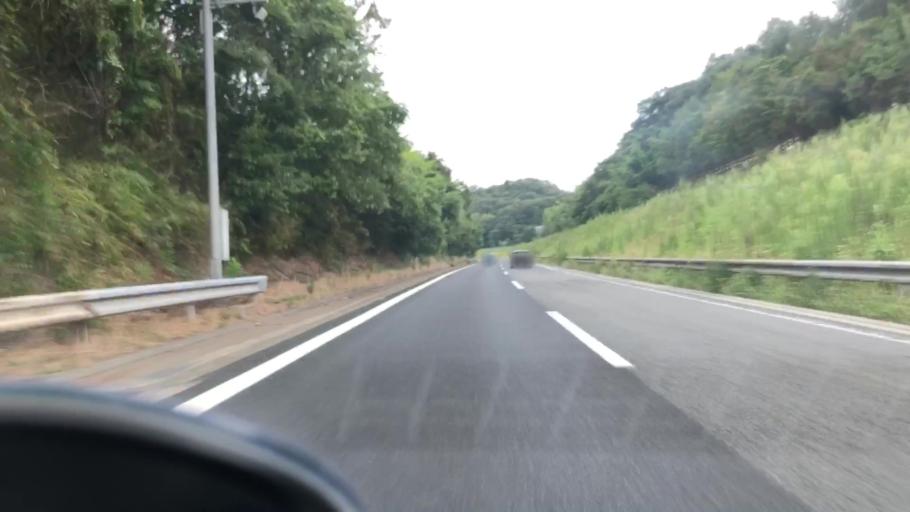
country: JP
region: Hyogo
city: Sandacho
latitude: 34.8908
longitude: 135.1271
